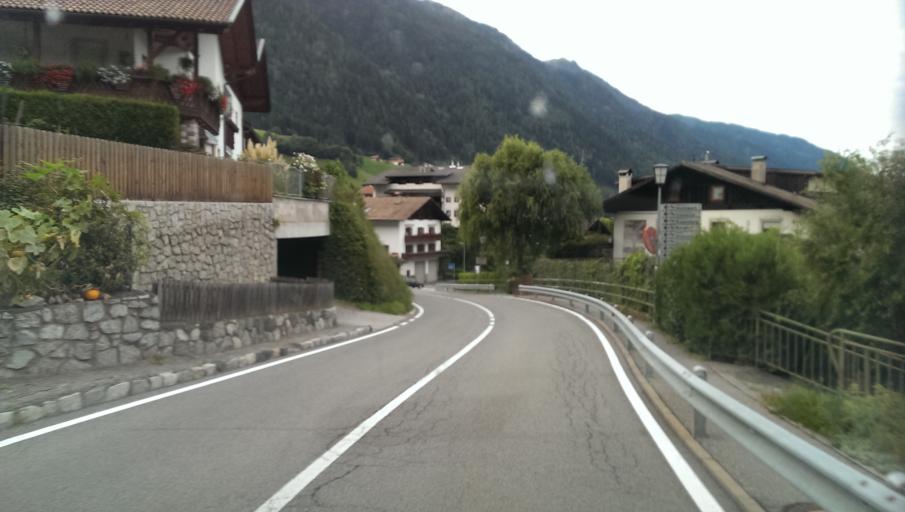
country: IT
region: Trentino-Alto Adige
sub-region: Bolzano
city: San Leonardo in Passiria
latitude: 46.8165
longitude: 11.2448
